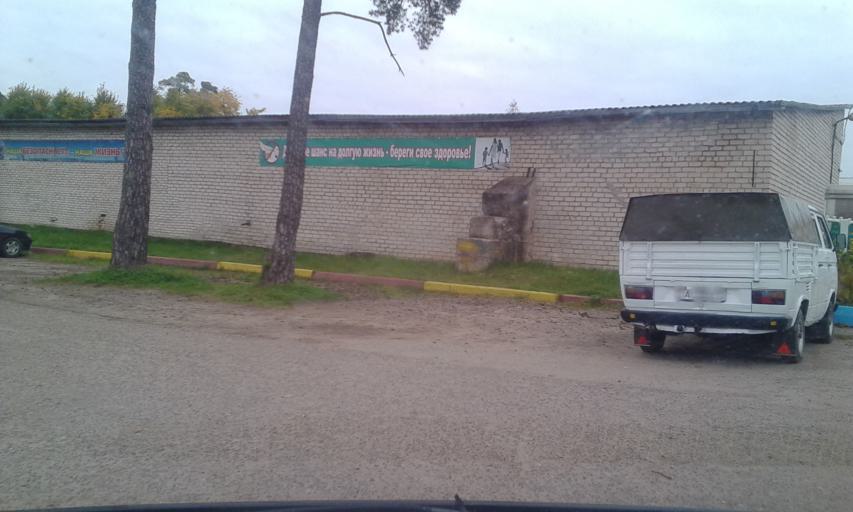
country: BY
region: Vitebsk
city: Pastavy
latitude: 55.1162
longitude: 26.8718
